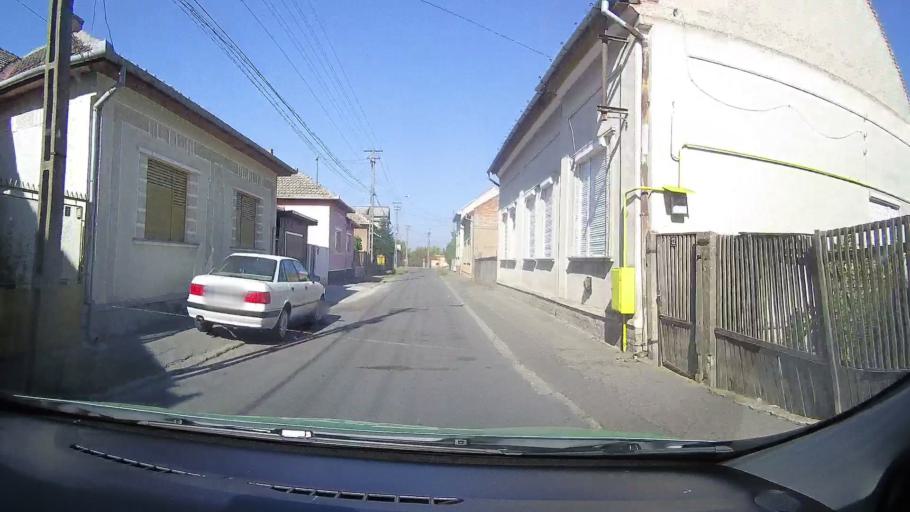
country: RO
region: Satu Mare
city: Carei
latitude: 47.6907
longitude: 22.4677
